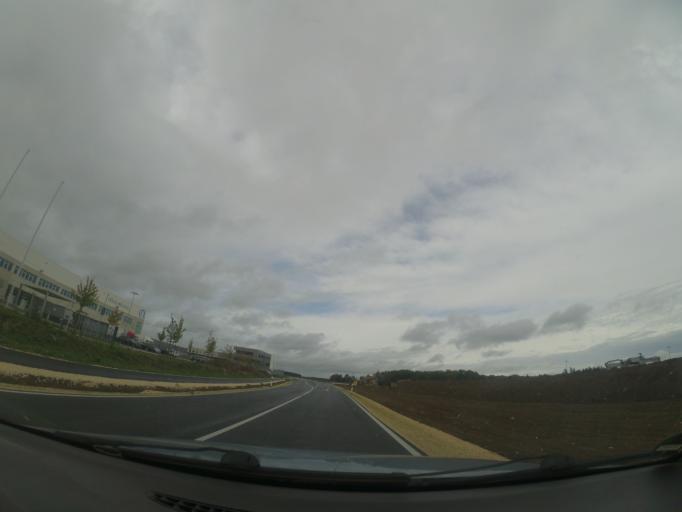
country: DE
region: Baden-Wuerttemberg
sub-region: Tuebingen Region
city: Beimerstetten
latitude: 48.4624
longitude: 9.9720
